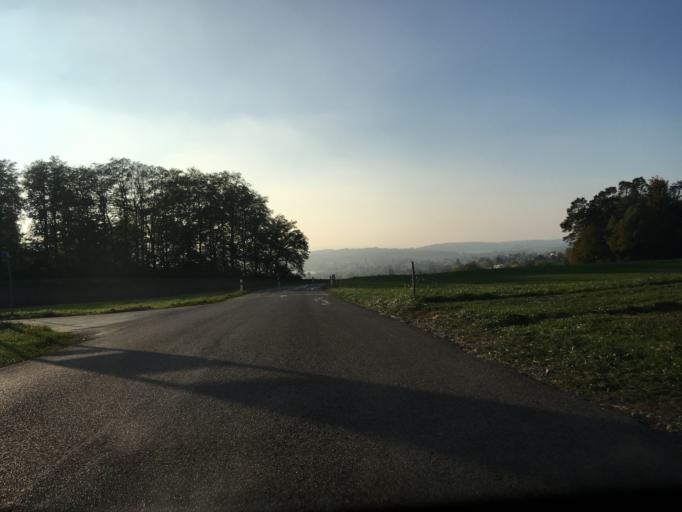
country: CH
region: Zurich
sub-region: Bezirk Pfaeffikon
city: Hittnau / Hittnau (Dorf)
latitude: 47.3610
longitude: 8.8098
